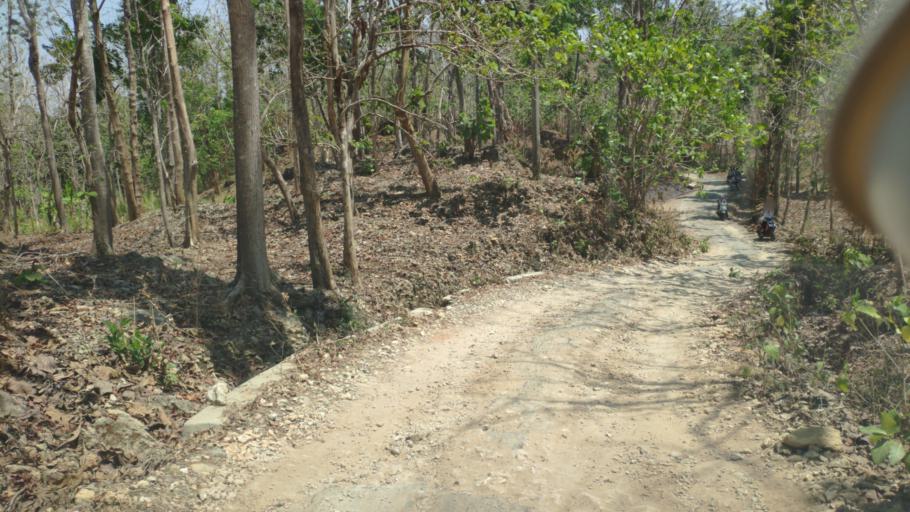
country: ID
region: Central Java
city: Guyangan
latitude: -6.9461
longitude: 111.1220
